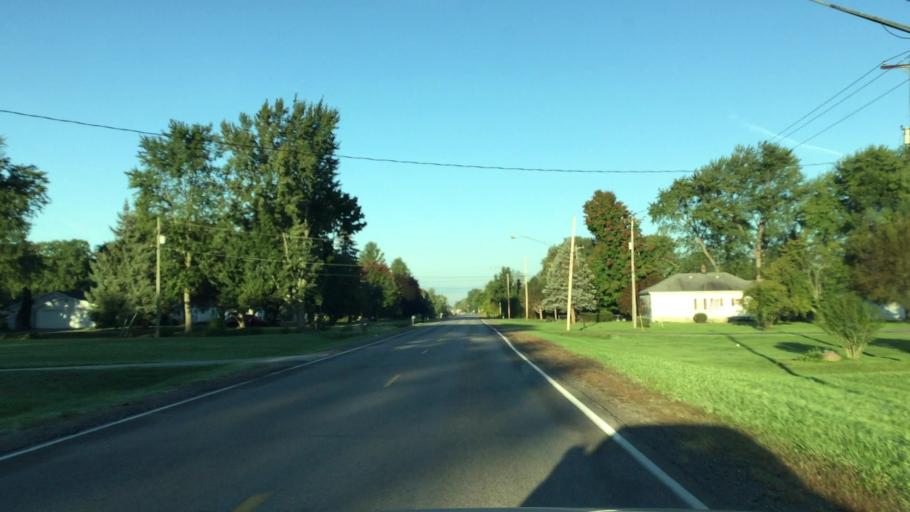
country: US
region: Michigan
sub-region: Genesee County
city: Beecher
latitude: 43.0900
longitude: -83.7458
